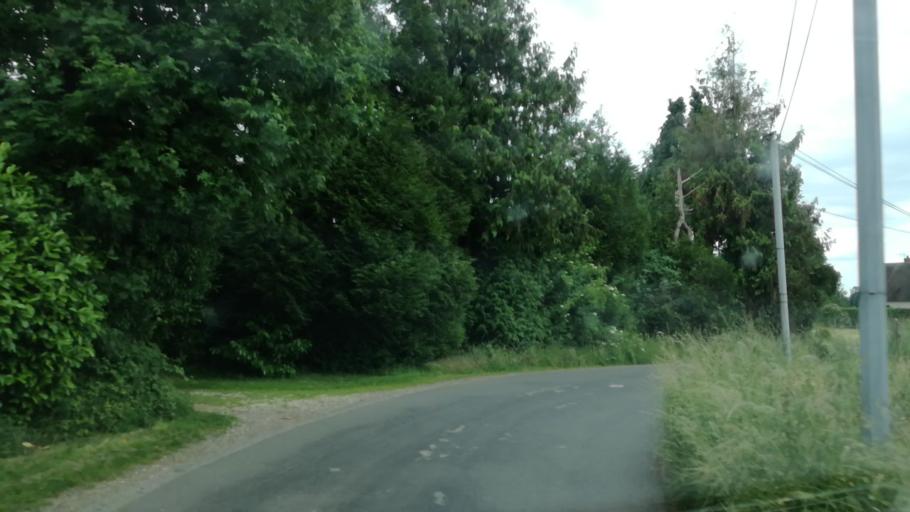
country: FR
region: Haute-Normandie
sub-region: Departement de l'Eure
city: Bourg-Achard
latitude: 49.2990
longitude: 0.8055
